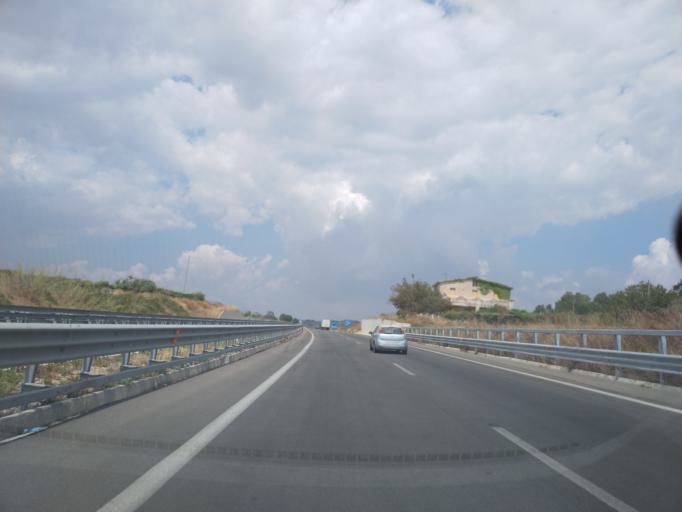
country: IT
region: Sicily
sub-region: Agrigento
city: Grotte
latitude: 37.3650
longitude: 13.7040
